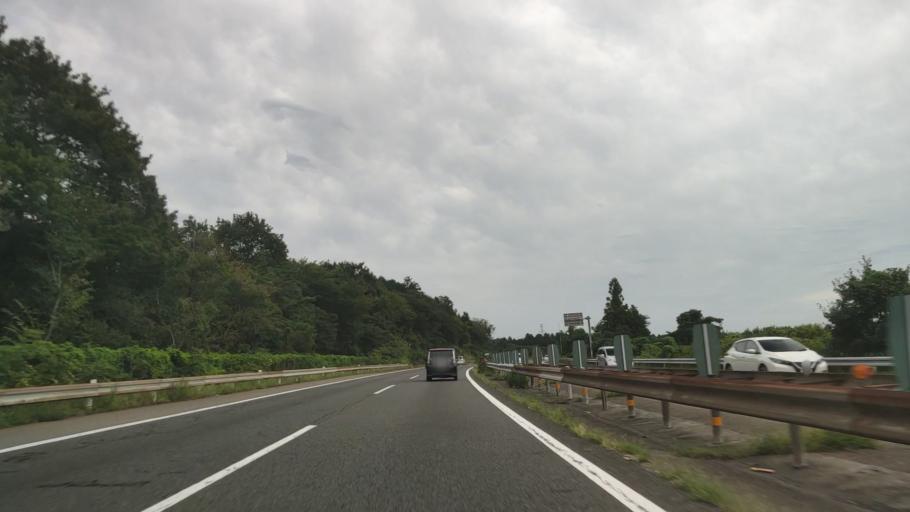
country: JP
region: Shiga Prefecture
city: Youkaichi
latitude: 35.1414
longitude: 136.2810
